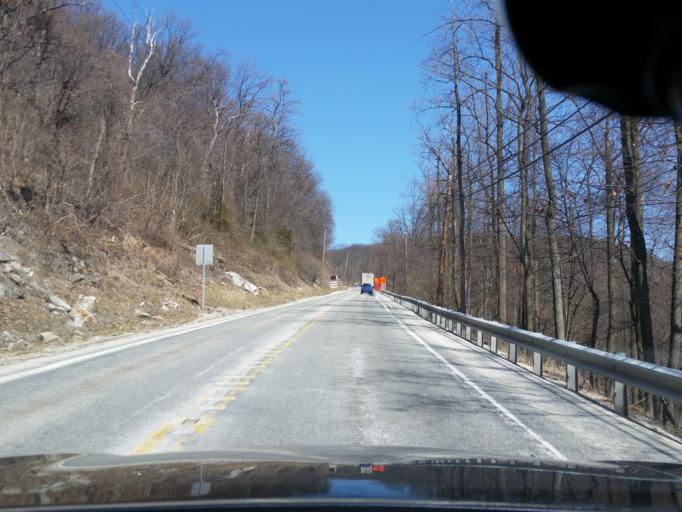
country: US
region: Pennsylvania
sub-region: Cumberland County
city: Schlusser
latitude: 40.2914
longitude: -77.1360
